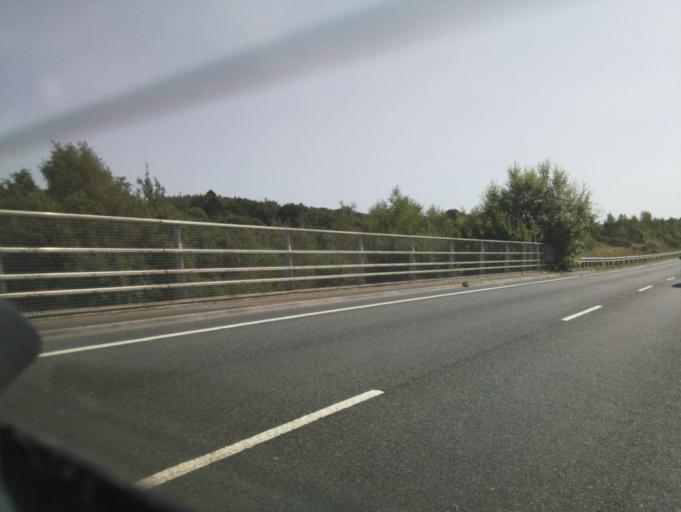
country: GB
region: Wales
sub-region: Caerphilly County Borough
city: Bargoed
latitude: 51.6794
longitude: -3.2227
